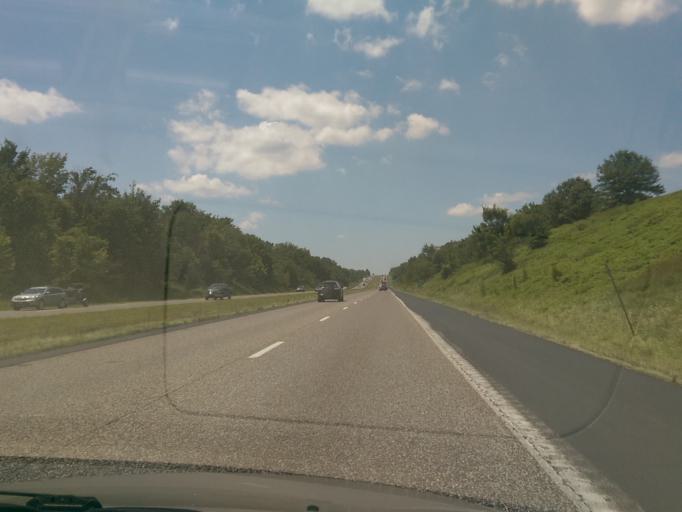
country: US
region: Missouri
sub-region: Cooper County
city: Boonville
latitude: 38.9387
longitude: -92.6492
